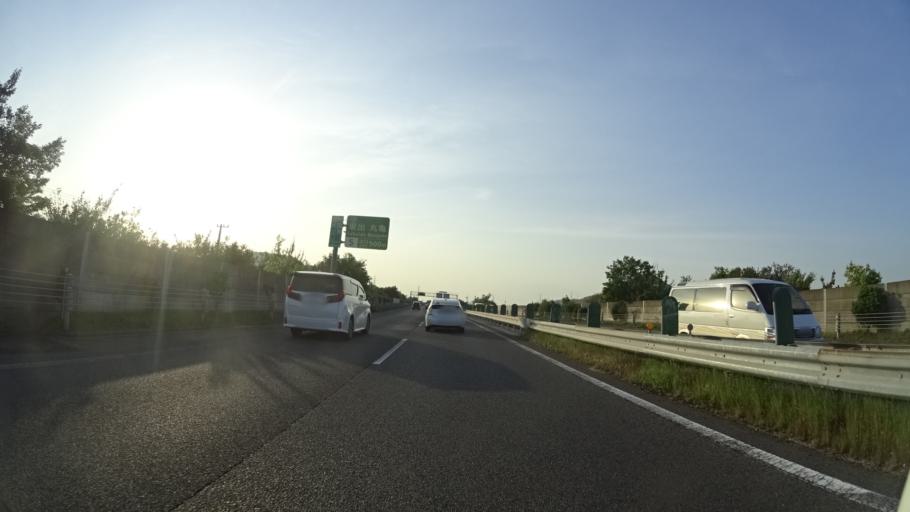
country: JP
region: Kagawa
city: Sakaidecho
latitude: 34.2905
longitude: 133.8497
